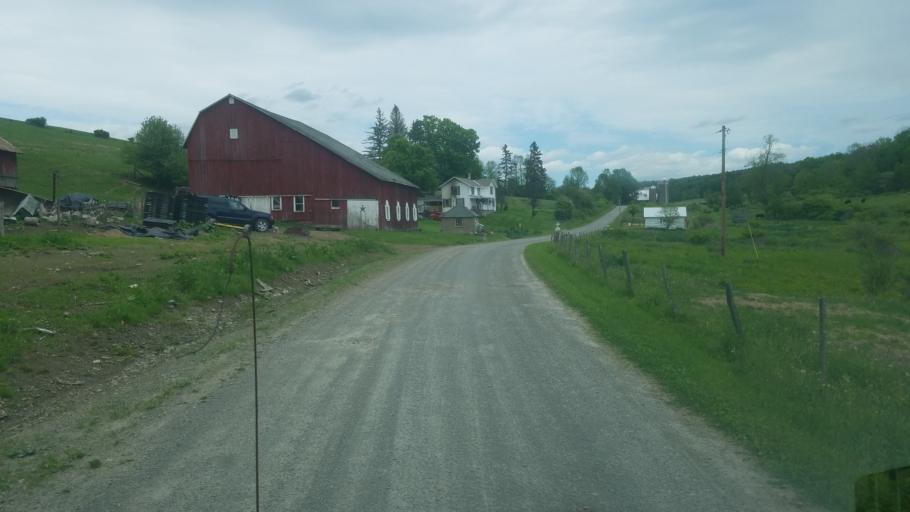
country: US
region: Pennsylvania
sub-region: Tioga County
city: Westfield
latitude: 41.8521
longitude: -77.6034
